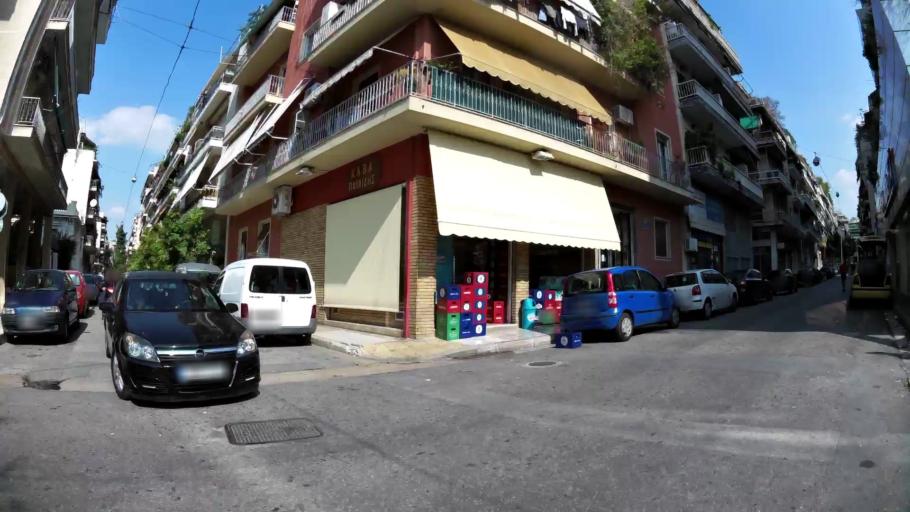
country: GR
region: Attica
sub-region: Nomarchia Athinas
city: Kipseli
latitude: 38.0104
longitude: 23.7323
